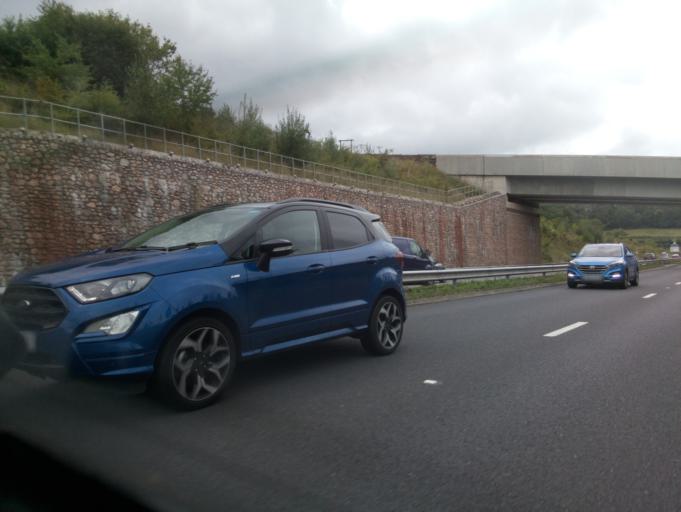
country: GB
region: England
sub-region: Devon
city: Kingskerswell
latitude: 50.4945
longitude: -3.5844
